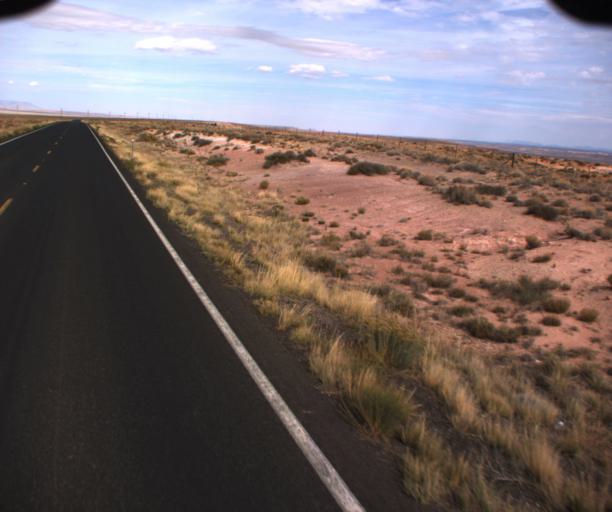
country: US
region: Arizona
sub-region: Apache County
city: Ganado
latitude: 35.8955
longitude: -109.6089
